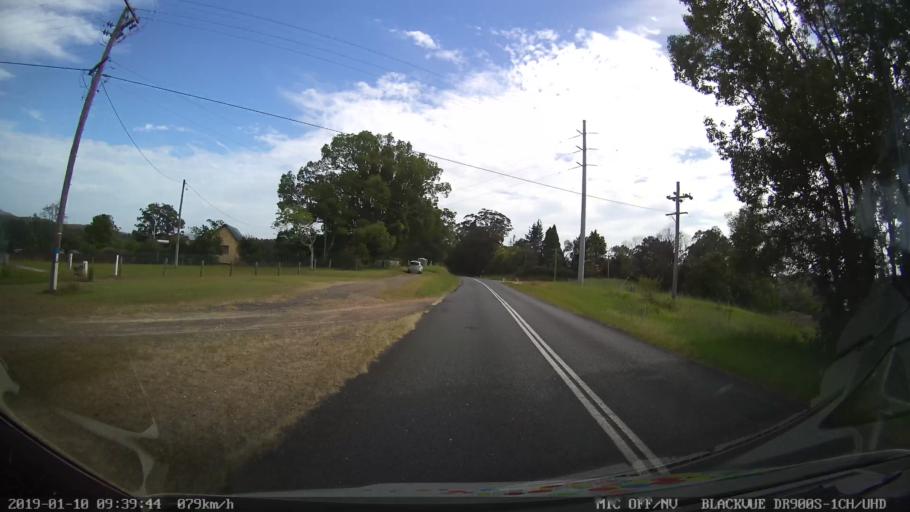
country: AU
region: New South Wales
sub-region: Coffs Harbour
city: Nana Glen
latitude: -30.1601
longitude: 153.0042
